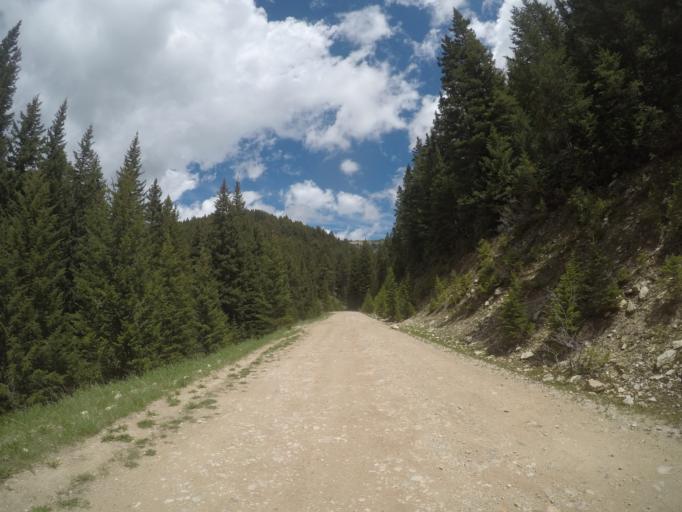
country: US
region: Wyoming
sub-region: Big Horn County
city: Lovell
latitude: 45.1705
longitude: -108.4123
